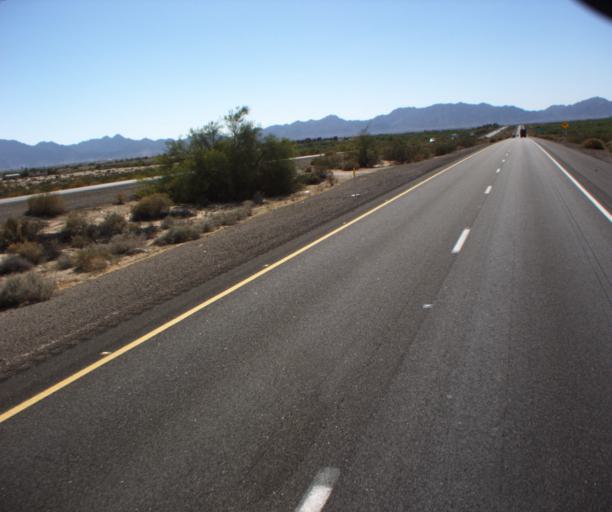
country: US
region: Arizona
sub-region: Yuma County
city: Wellton
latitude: 32.6592
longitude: -114.1542
